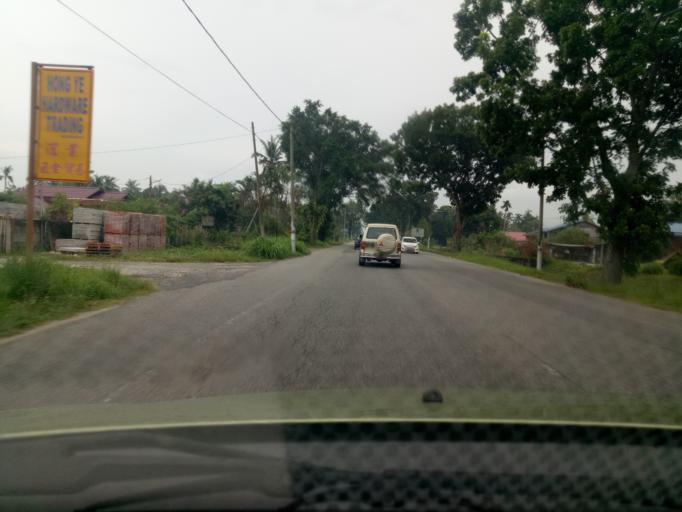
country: MY
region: Kedah
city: Gurun
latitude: 5.8981
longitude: 100.4370
